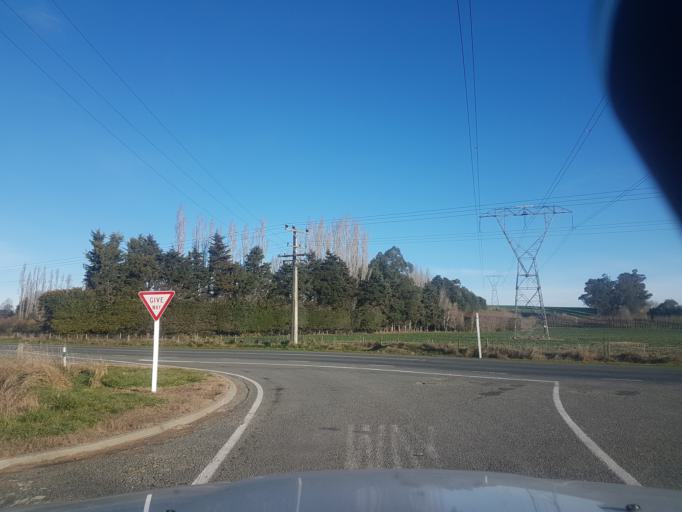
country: NZ
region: Canterbury
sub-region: Timaru District
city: Pleasant Point
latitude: -44.2779
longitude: 171.1704
